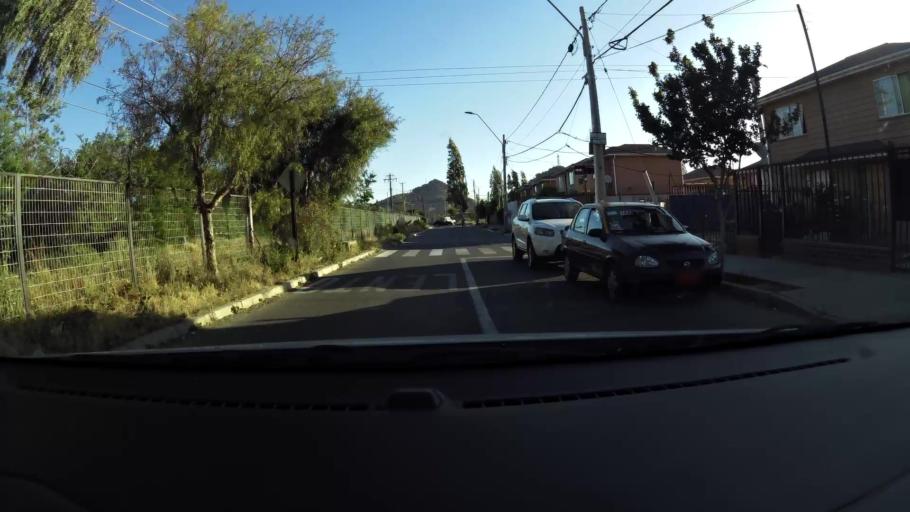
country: CL
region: Santiago Metropolitan
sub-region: Provincia de Maipo
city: San Bernardo
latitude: -33.6066
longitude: -70.6704
